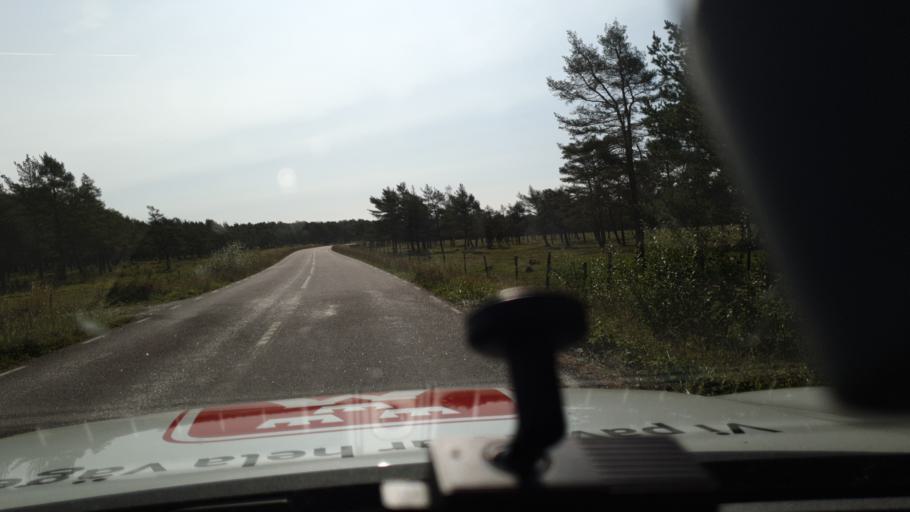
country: SE
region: Gotland
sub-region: Gotland
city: Hemse
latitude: 57.1033
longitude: 18.3002
